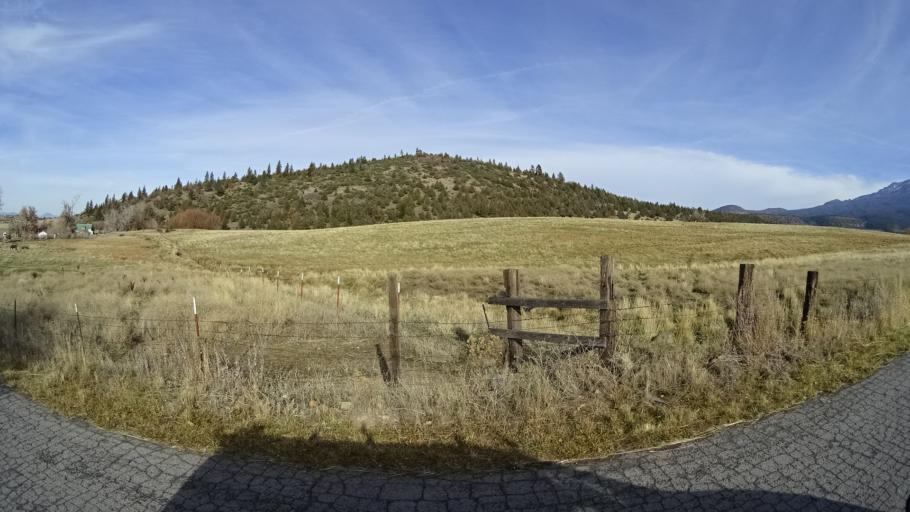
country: US
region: California
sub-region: Siskiyou County
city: Weed
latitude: 41.4621
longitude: -122.3865
